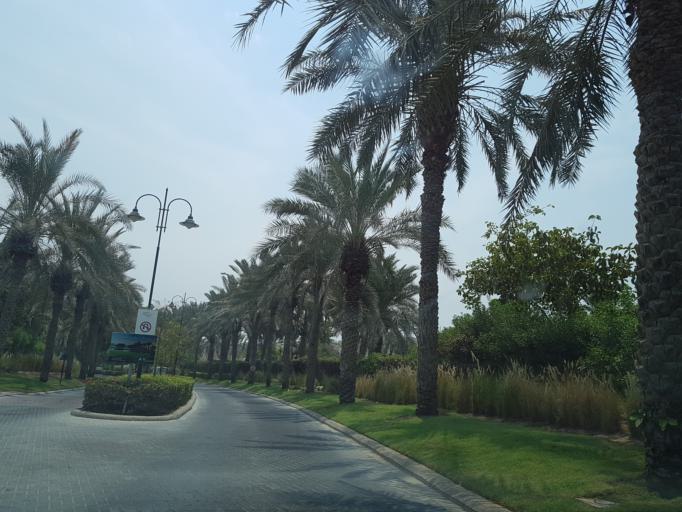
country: AE
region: Ash Shariqah
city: Sharjah
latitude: 25.2488
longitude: 55.3305
